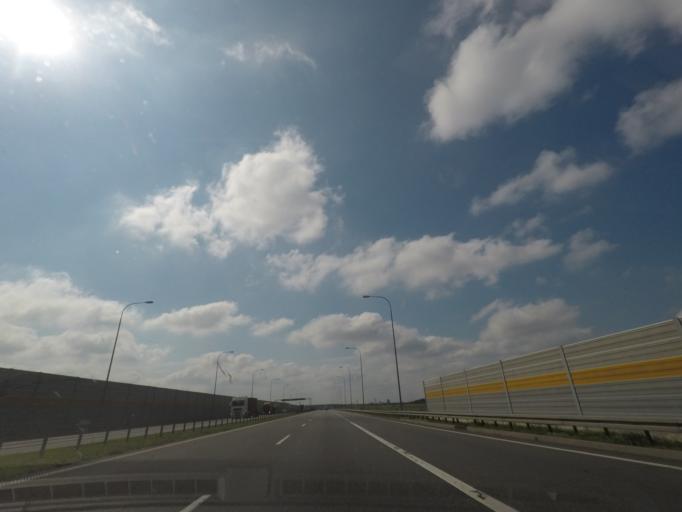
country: PL
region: Kujawsko-Pomorskie
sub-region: Powiat torunski
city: Lubicz Dolny
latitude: 53.0871
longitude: 18.7506
